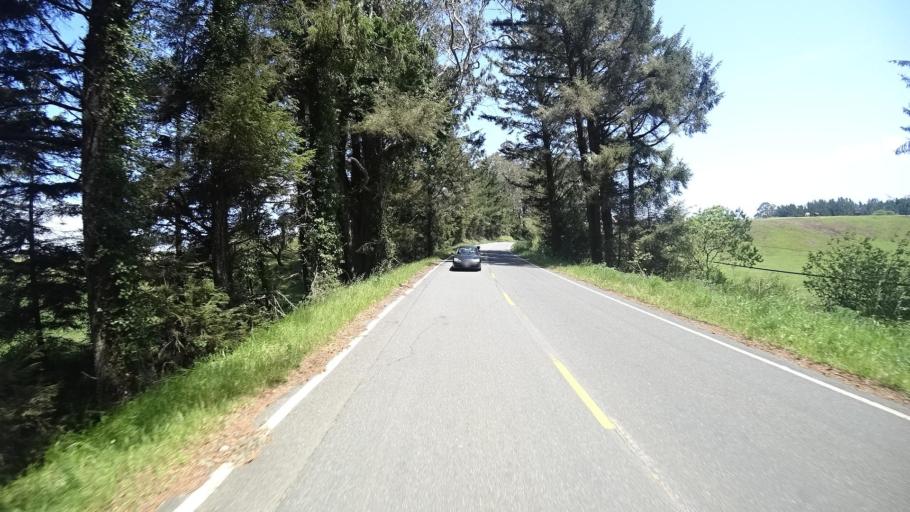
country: US
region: California
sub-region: Humboldt County
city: Humboldt Hill
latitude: 40.6538
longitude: -124.2201
